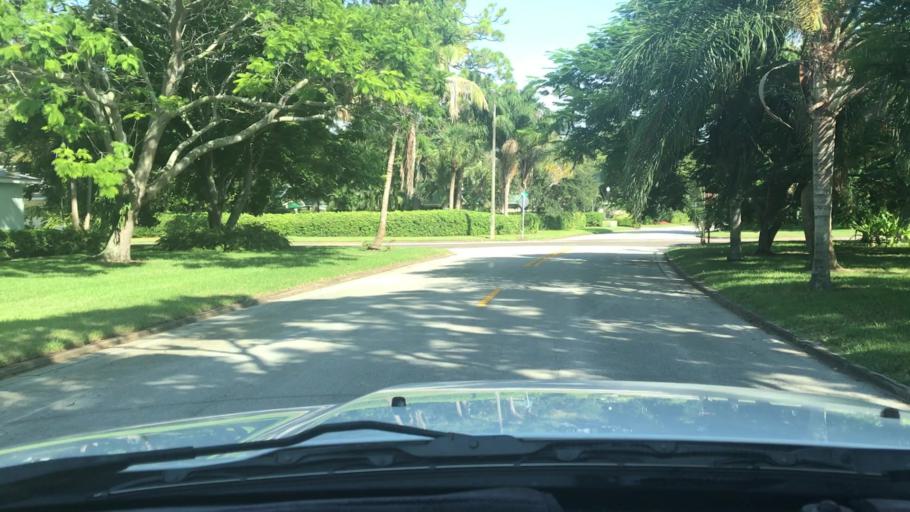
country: US
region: Florida
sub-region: Indian River County
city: Vero Beach
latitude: 27.6397
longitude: -80.4129
